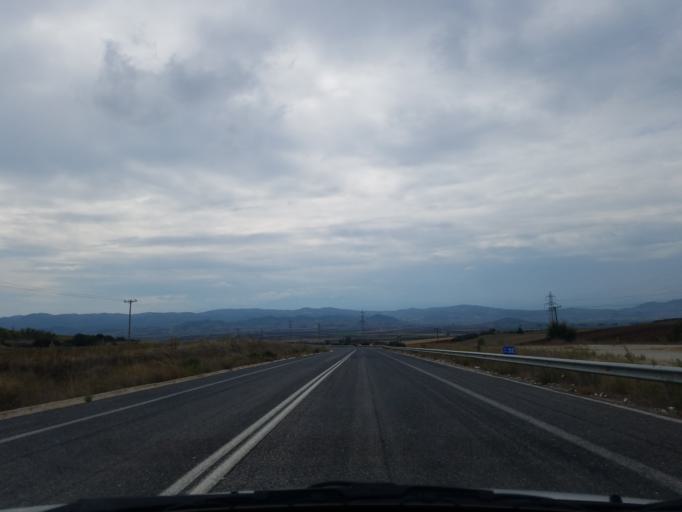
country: GR
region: Central Greece
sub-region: Nomos Fthiotidos
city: Domokos
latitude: 39.0974
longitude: 22.3050
